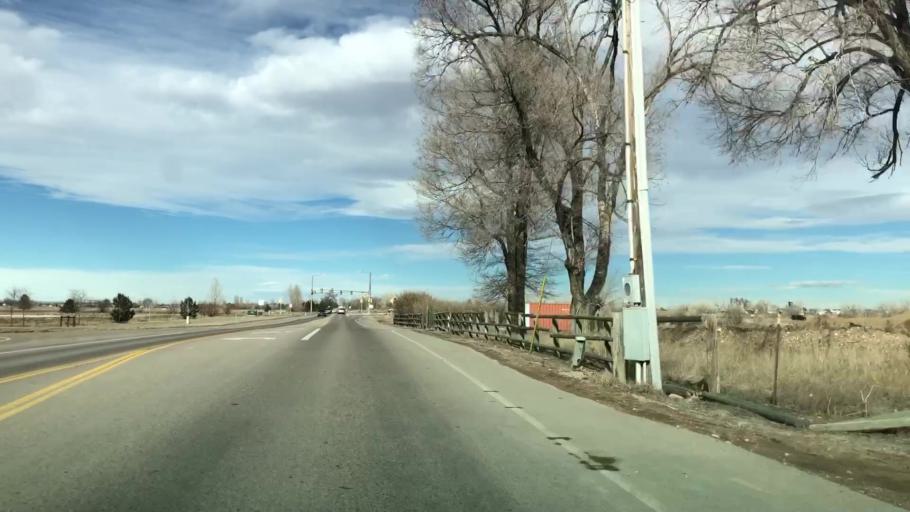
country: US
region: Colorado
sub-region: Weld County
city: Windsor
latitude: 40.4769
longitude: -104.9441
